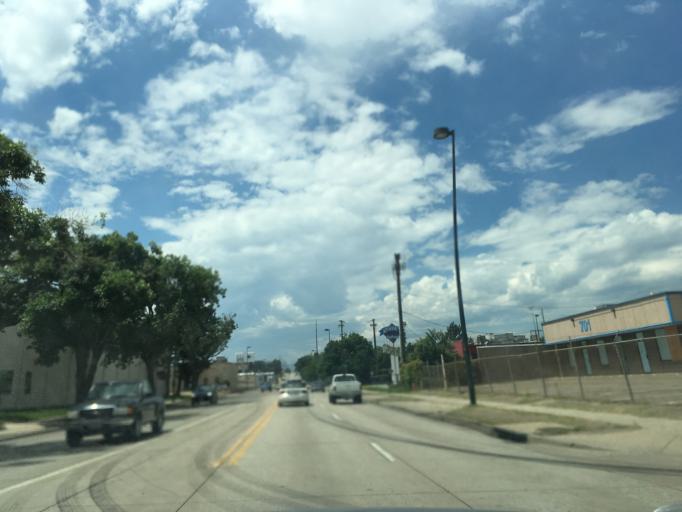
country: US
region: Colorado
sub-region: Denver County
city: Denver
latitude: 39.6967
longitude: -104.9956
